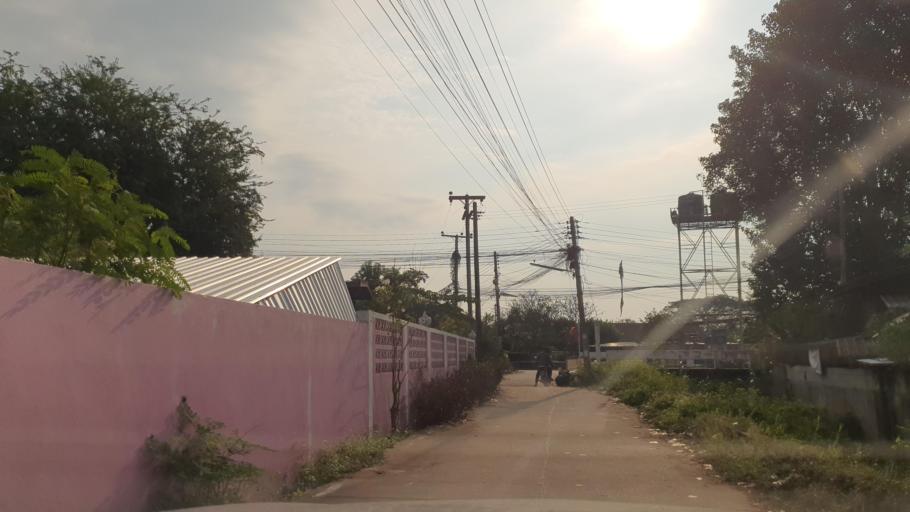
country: TH
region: Chiang Mai
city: San Kamphaeng
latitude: 18.7363
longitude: 99.1040
